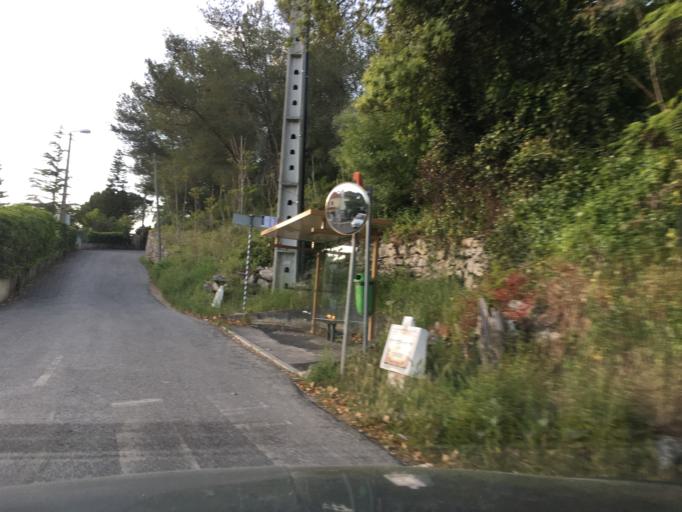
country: PT
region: Lisbon
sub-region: Oeiras
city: Barcarena
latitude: 38.7265
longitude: -9.2763
